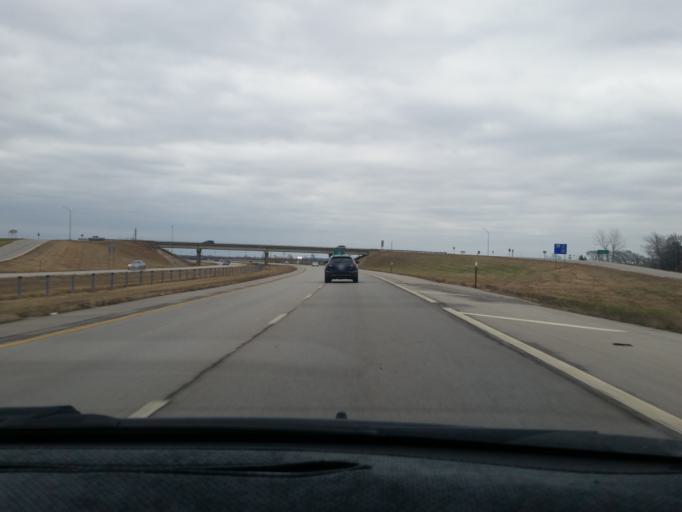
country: US
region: Kansas
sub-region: Douglas County
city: Eudora
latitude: 38.9289
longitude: -95.0980
